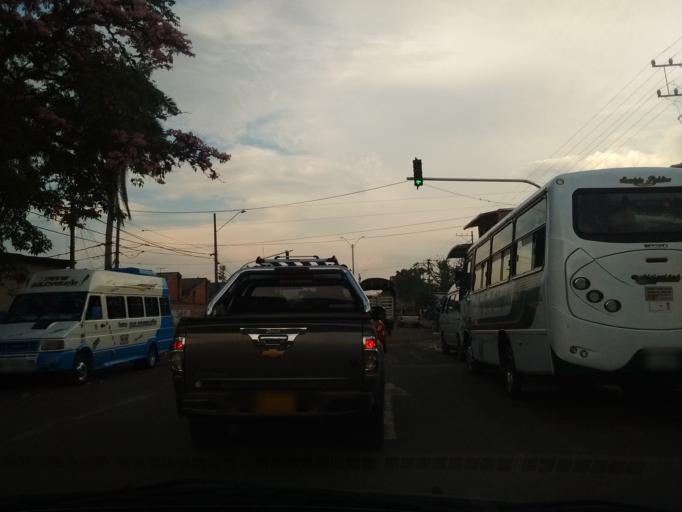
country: CO
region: Cauca
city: Santander de Quilichao
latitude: 3.0066
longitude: -76.4869
